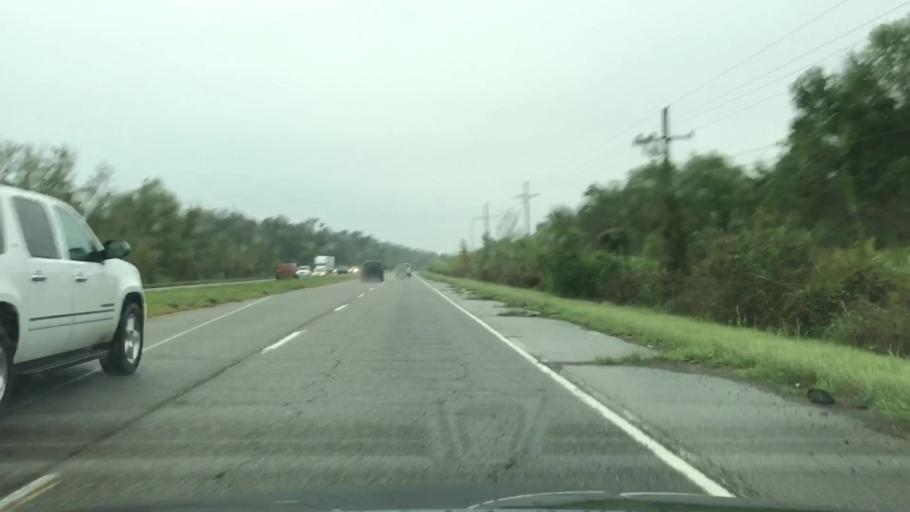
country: US
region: Louisiana
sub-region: Saint Charles Parish
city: Des Allemands
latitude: 29.7914
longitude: -90.5124
